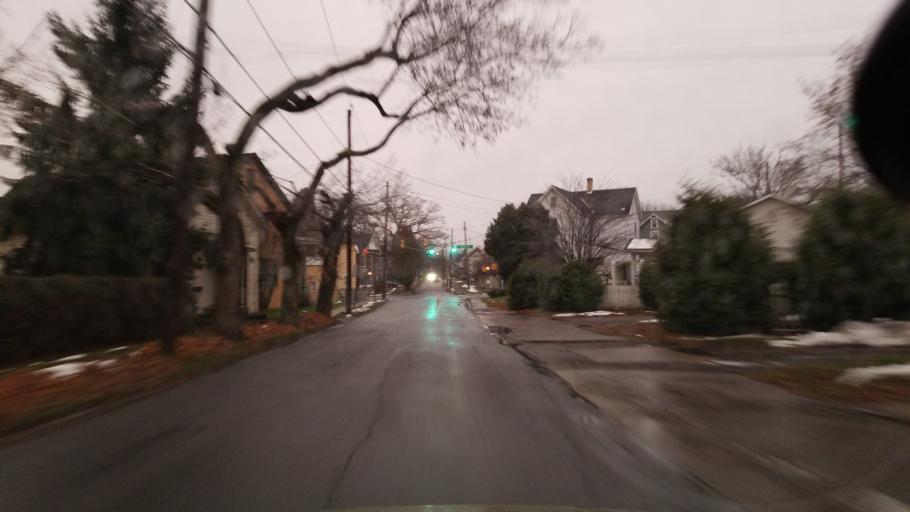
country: US
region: Pennsylvania
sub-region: Clearfield County
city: Clearfield
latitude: 41.0279
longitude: -78.4477
